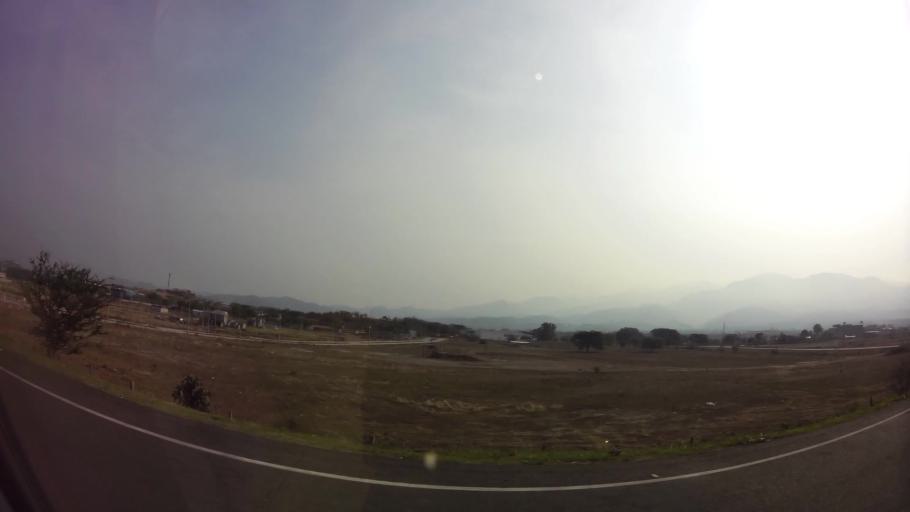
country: HN
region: Comayagua
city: Comayagua
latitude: 14.4249
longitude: -87.6328
